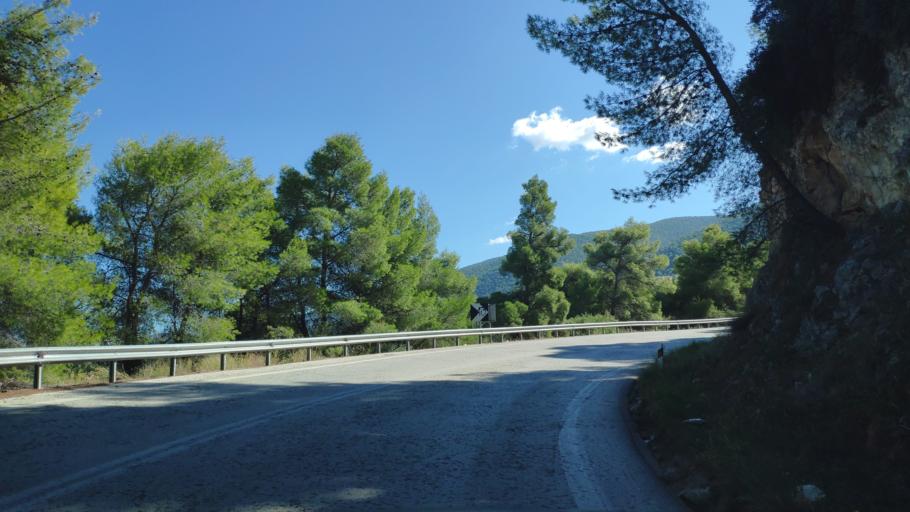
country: GR
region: Peloponnese
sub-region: Nomos Korinthias
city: Loutra Oraias Elenis
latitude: 37.8336
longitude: 23.0250
